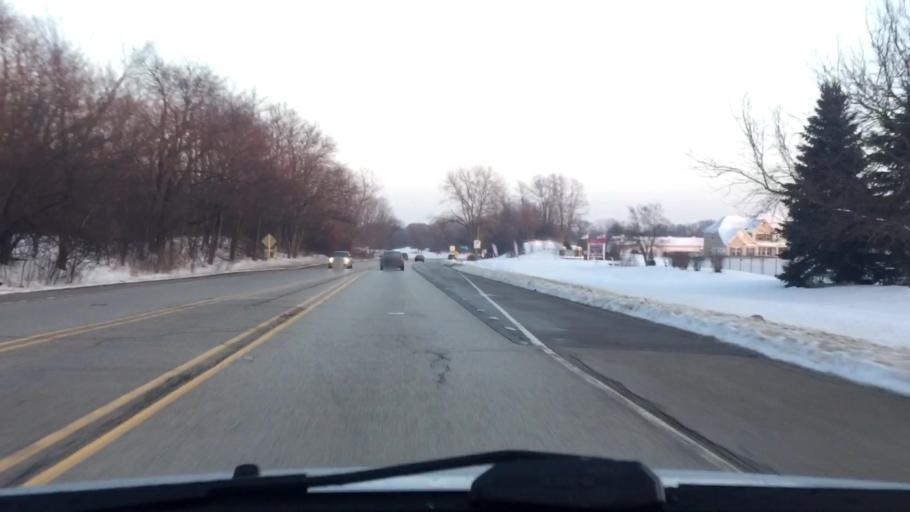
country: US
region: Illinois
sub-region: Kane County
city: Village of Campton Hills
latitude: 41.9343
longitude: -88.3865
